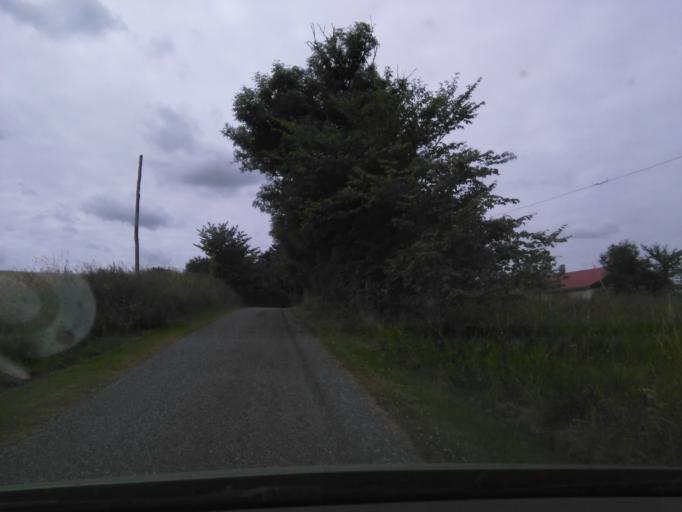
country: DK
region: Central Jutland
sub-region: Arhus Kommune
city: Solbjerg
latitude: 55.9938
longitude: 10.0459
